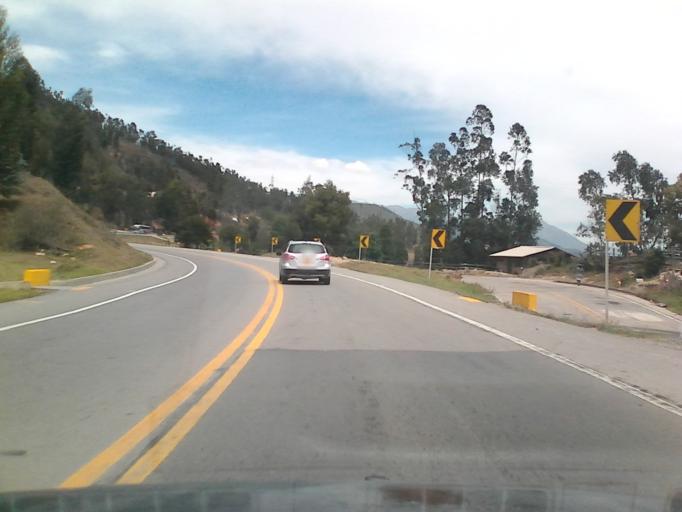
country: CO
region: Boyaca
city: Tibasosa
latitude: 5.7608
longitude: -72.9958
